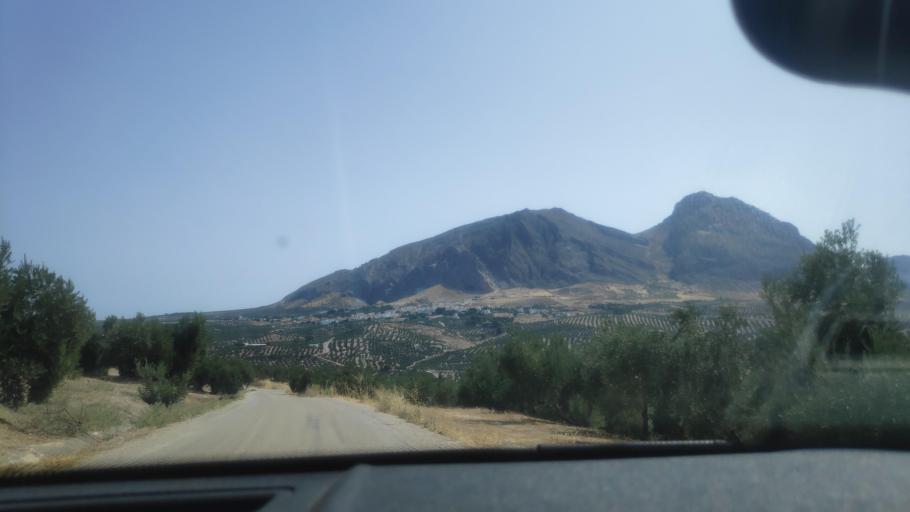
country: ES
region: Andalusia
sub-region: Provincia de Jaen
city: Jimena
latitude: 37.8068
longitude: -3.4346
